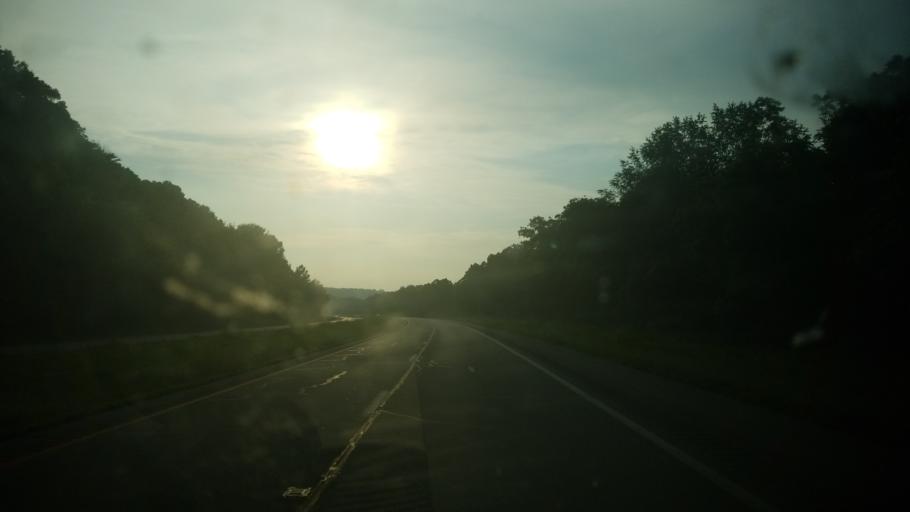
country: US
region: Ohio
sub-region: Pike County
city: Piketon
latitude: 39.0590
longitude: -83.0719
